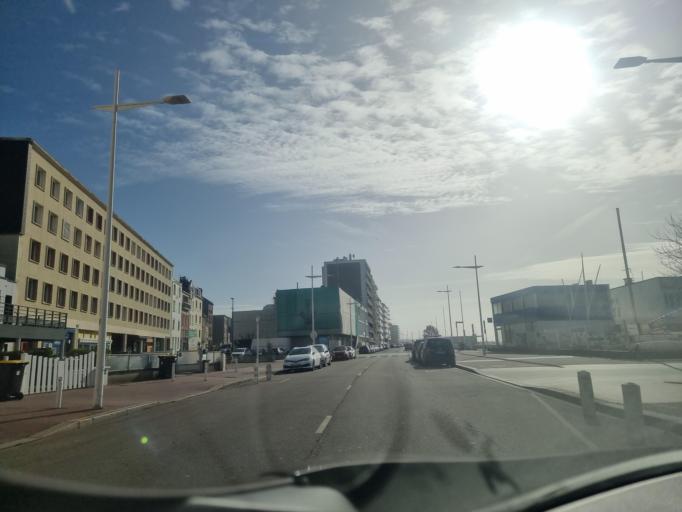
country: FR
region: Haute-Normandie
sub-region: Departement de la Seine-Maritime
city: Le Havre
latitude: 49.4924
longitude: 0.0966
